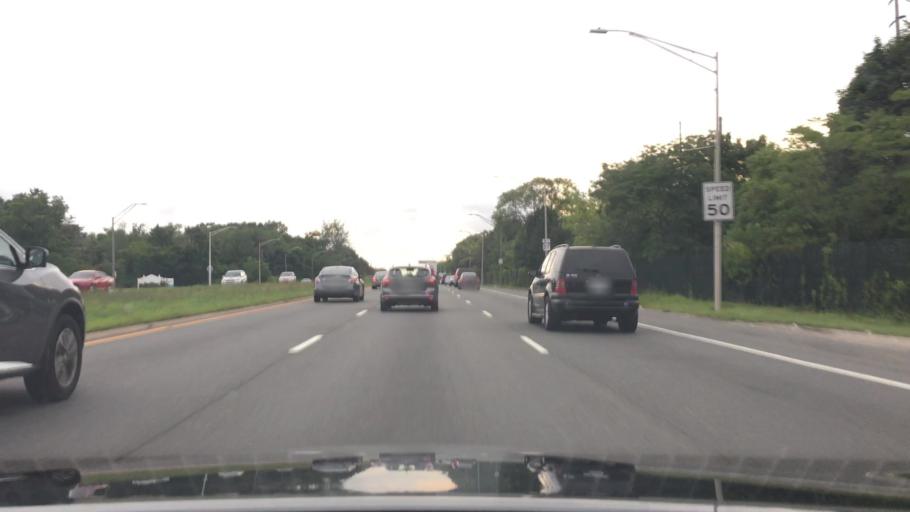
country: US
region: New York
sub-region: Nassau County
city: Bellmore
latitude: 40.6664
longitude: -73.5380
